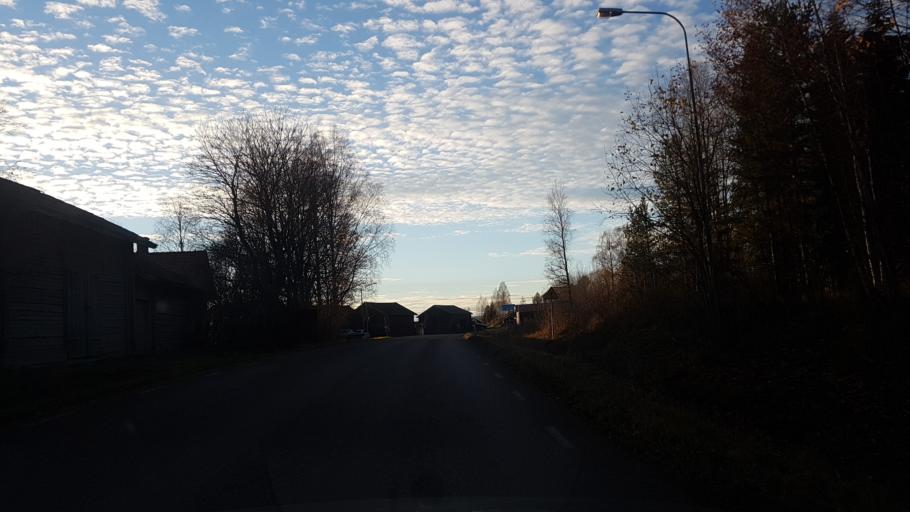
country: SE
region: Dalarna
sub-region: Leksand Municipality
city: Smedby
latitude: 60.7159
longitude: 15.0902
